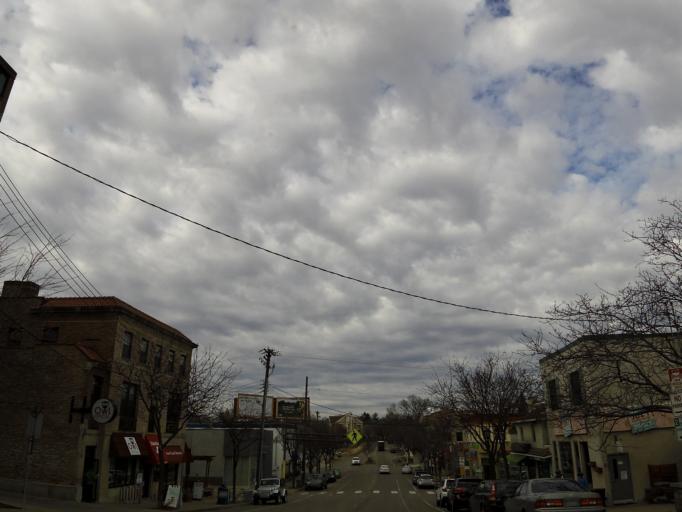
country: US
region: Minnesota
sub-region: Hennepin County
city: Saint Louis Park
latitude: 44.9235
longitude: -93.3150
